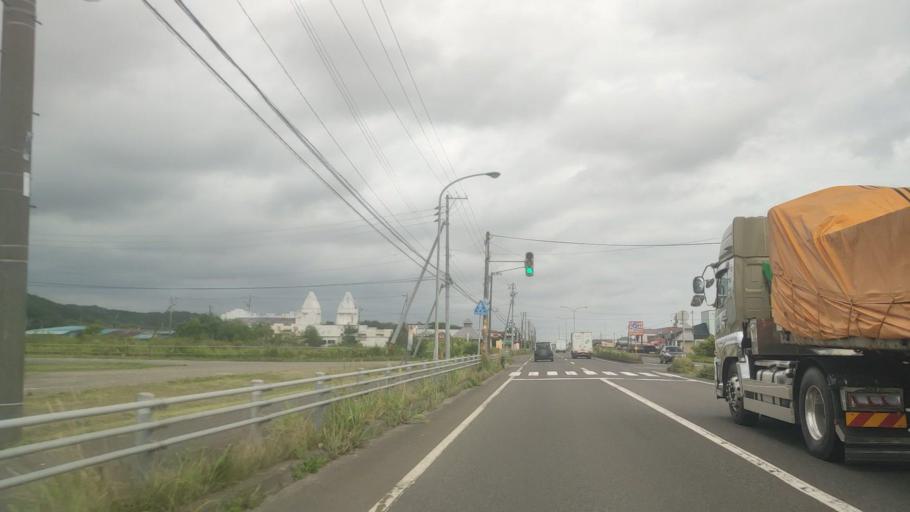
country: JP
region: Hokkaido
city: Shiraoi
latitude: 42.4720
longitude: 141.2327
